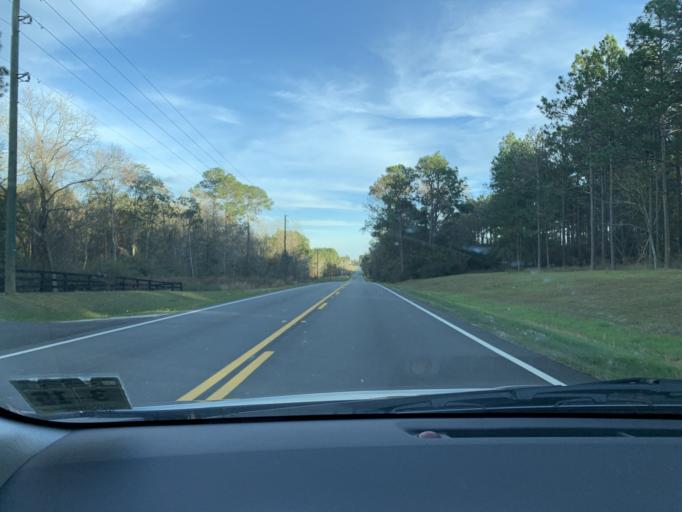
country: US
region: Georgia
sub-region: Irwin County
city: Ocilla
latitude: 31.5821
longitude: -83.0669
